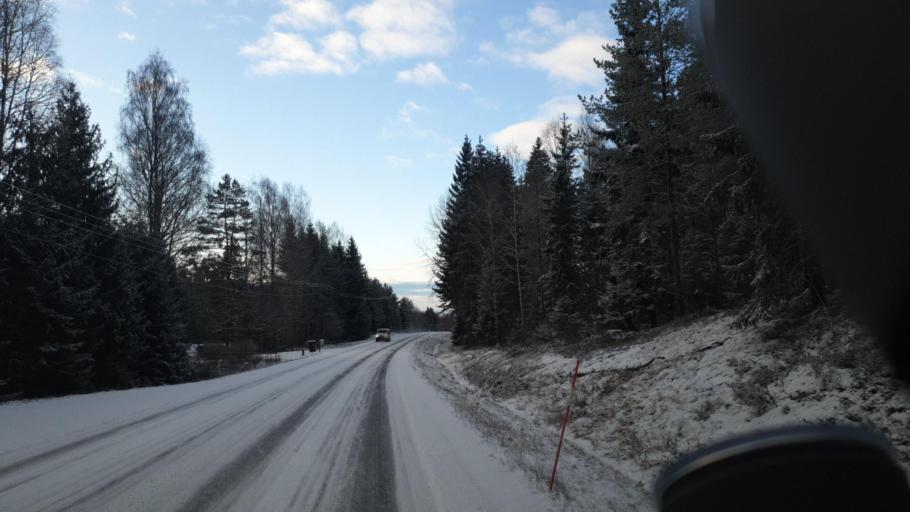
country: SE
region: Vaermland
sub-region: Arvika Kommun
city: Arvika
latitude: 59.7150
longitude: 12.5689
